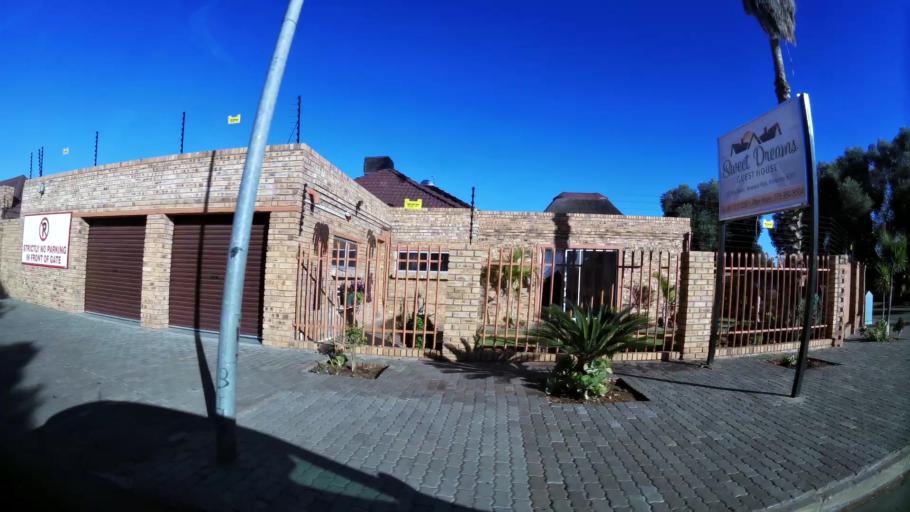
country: ZA
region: Northern Cape
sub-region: Frances Baard District Municipality
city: Kimberley
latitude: -28.7380
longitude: 24.7353
